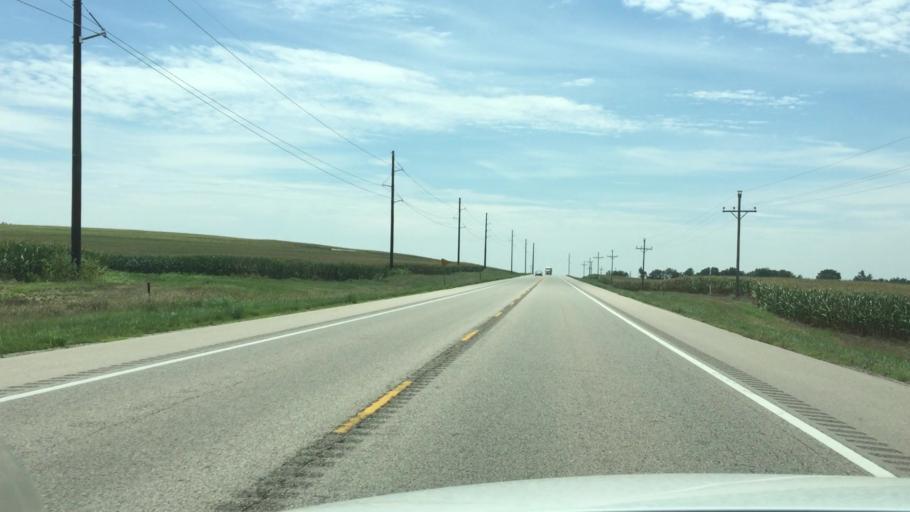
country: US
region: Kansas
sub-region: Nemaha County
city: Sabetha
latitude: 39.8254
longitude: -95.7310
